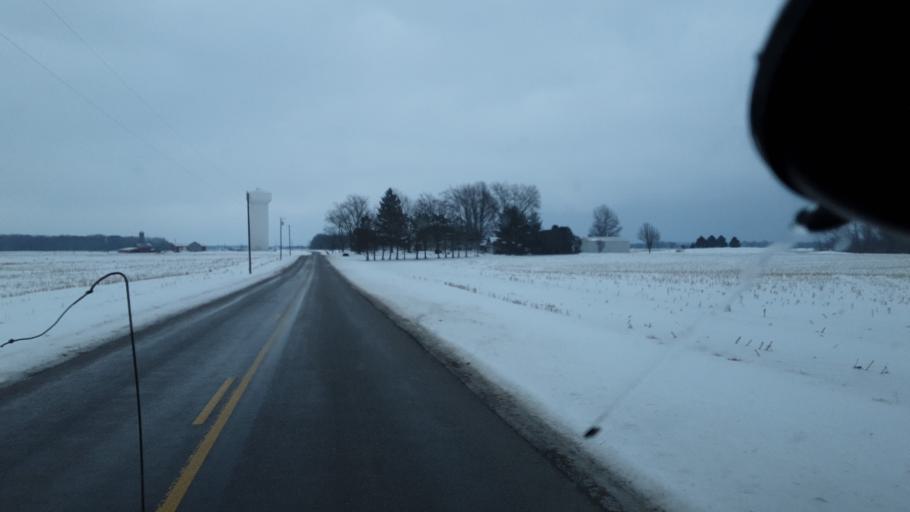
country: US
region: Ohio
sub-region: Union County
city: New California
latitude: 40.1863
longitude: -83.2931
